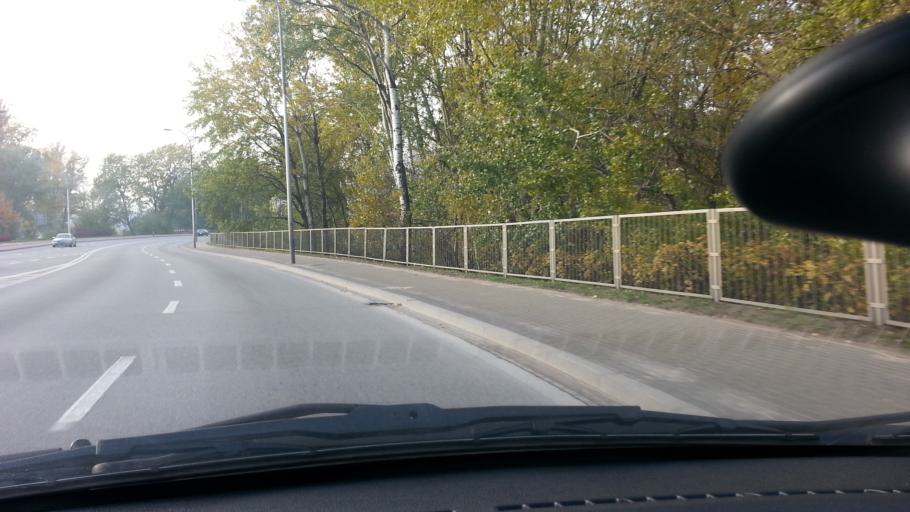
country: PL
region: Masovian Voivodeship
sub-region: Warszawa
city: Praga Polnoc
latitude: 52.2441
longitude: 21.0375
